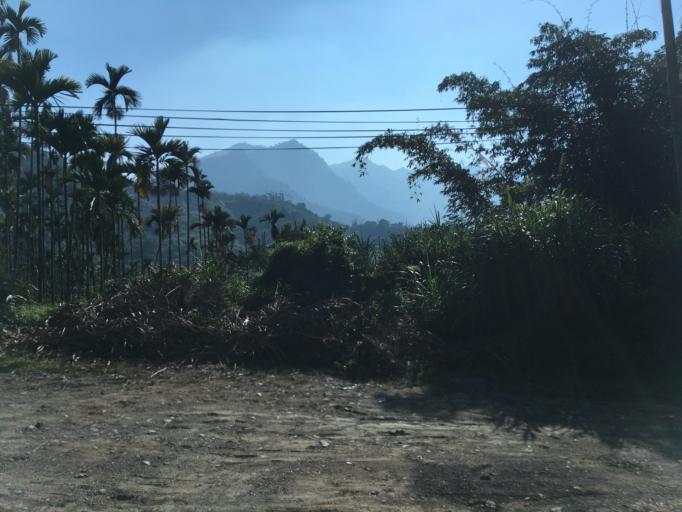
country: TW
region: Taiwan
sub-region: Chiayi
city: Jiayi Shi
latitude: 23.4342
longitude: 120.6322
